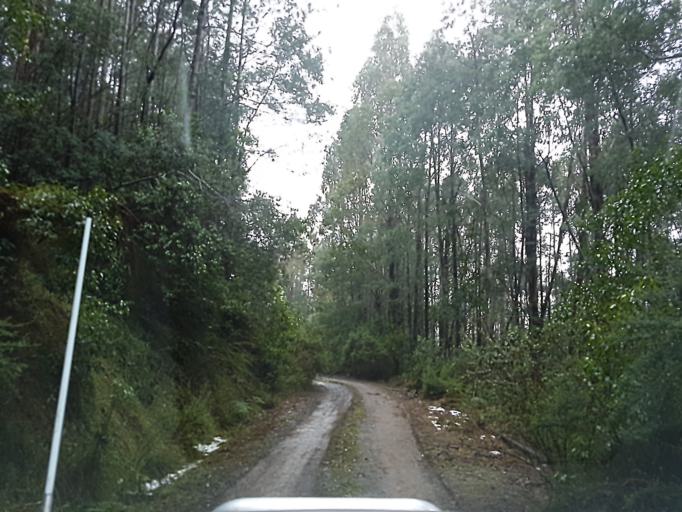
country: AU
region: Victoria
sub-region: Yarra Ranges
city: Millgrove
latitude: -37.5457
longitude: 145.8960
